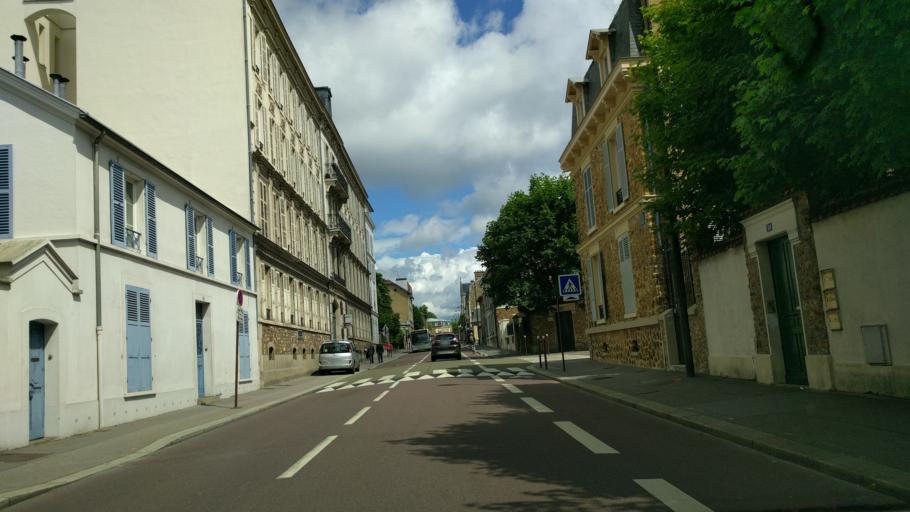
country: FR
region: Ile-de-France
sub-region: Departement des Yvelines
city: Le Chesnay
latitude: 48.8157
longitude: 2.1364
